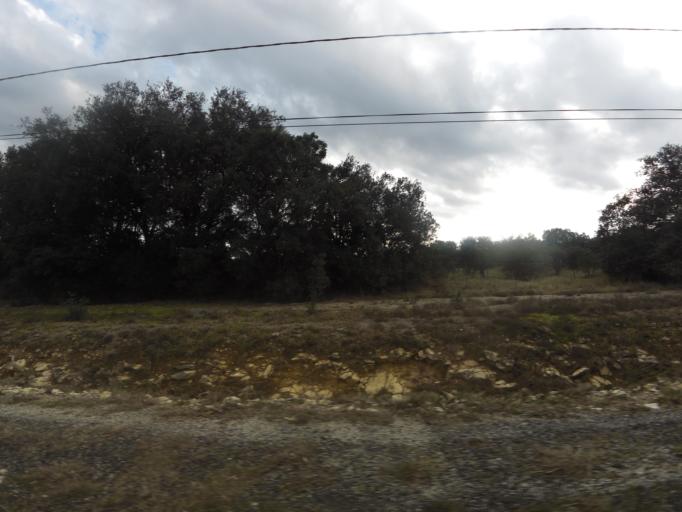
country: FR
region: Languedoc-Roussillon
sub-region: Departement du Gard
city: Saint-Mamert-du-Gard
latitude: 43.8583
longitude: 4.1915
